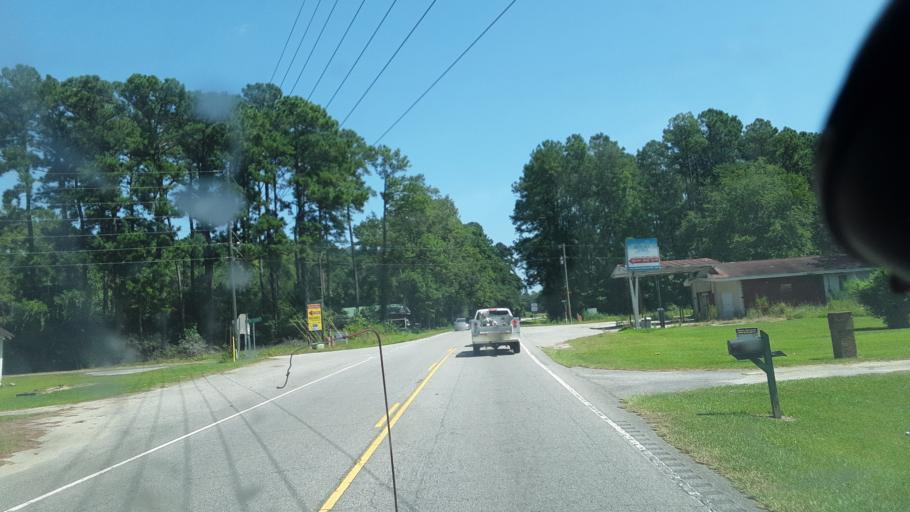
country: US
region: South Carolina
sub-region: Horry County
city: Forestbrook
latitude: 33.8348
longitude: -78.8823
